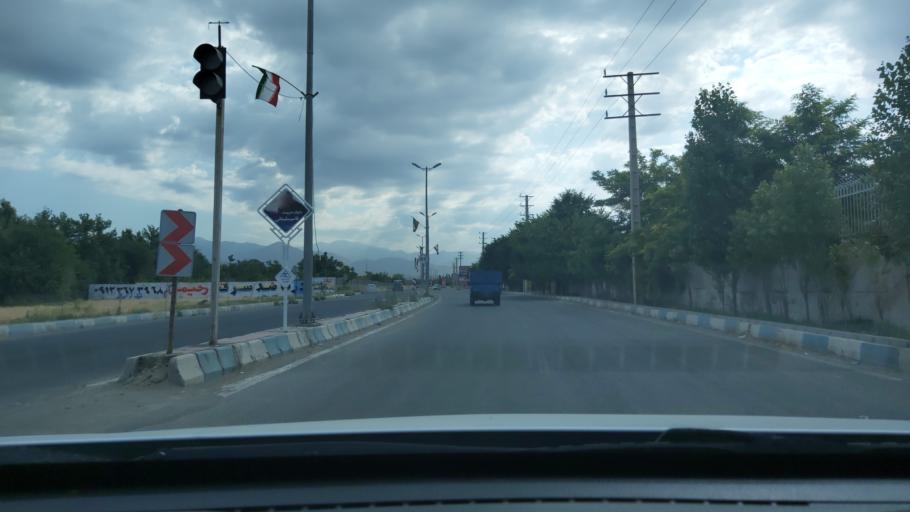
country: IR
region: Alborz
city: Hashtgerd
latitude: 35.9371
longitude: 50.7607
